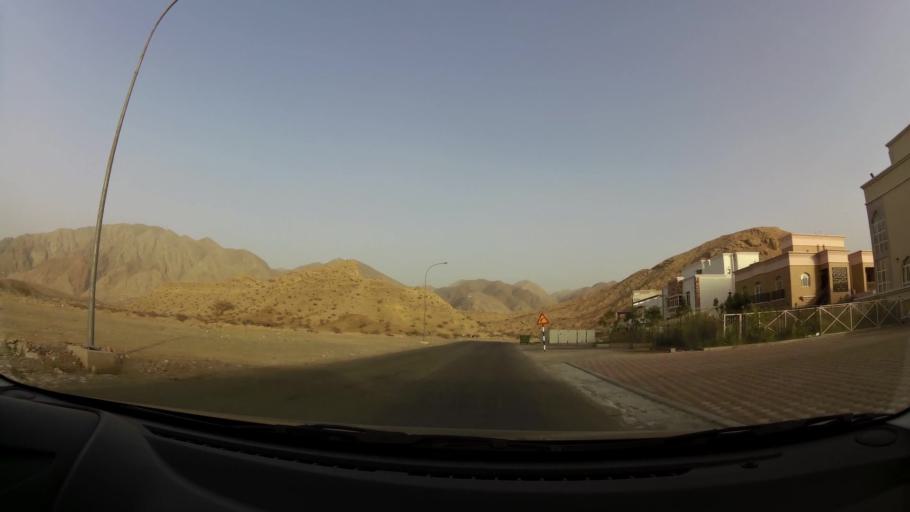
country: OM
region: Muhafazat Masqat
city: Bawshar
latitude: 23.5084
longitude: 58.3480
